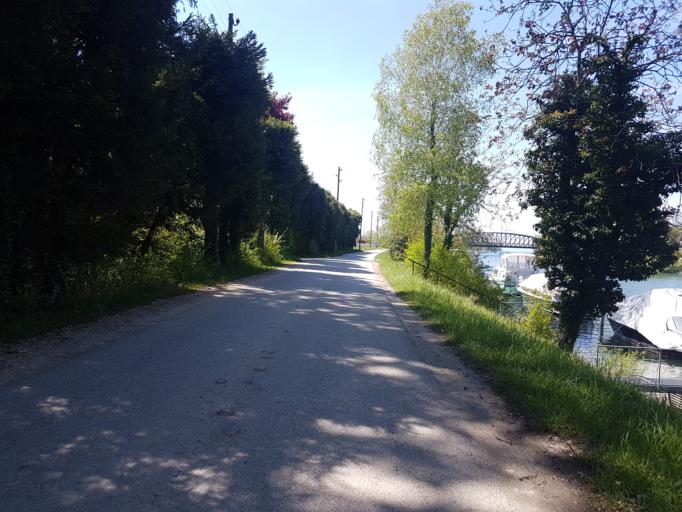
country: CH
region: Neuchatel
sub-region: Neuchatel District
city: Cornaux
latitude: 47.0121
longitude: 7.0322
